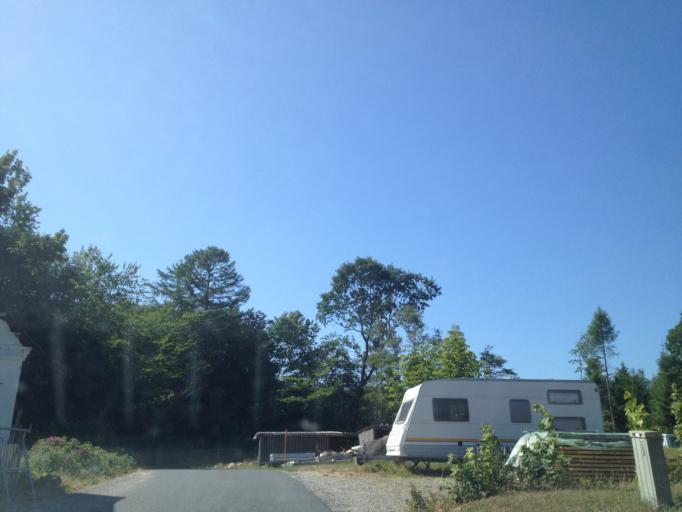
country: DK
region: Capital Region
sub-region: Helsingor Kommune
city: Hornbaek
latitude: 56.0143
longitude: 12.4691
